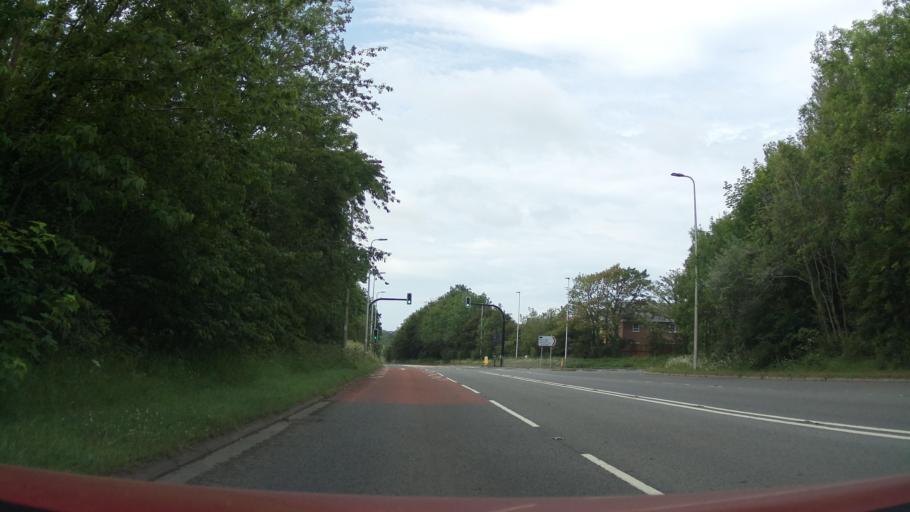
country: GB
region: Wales
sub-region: Vale of Glamorgan
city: Llantwit Major
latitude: 51.4048
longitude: -3.4550
